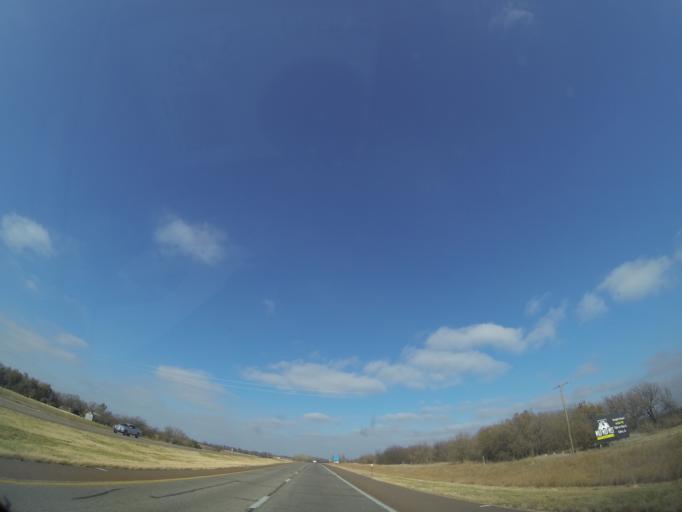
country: US
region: Kansas
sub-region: McPherson County
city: McPherson
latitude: 38.4631
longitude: -97.6208
